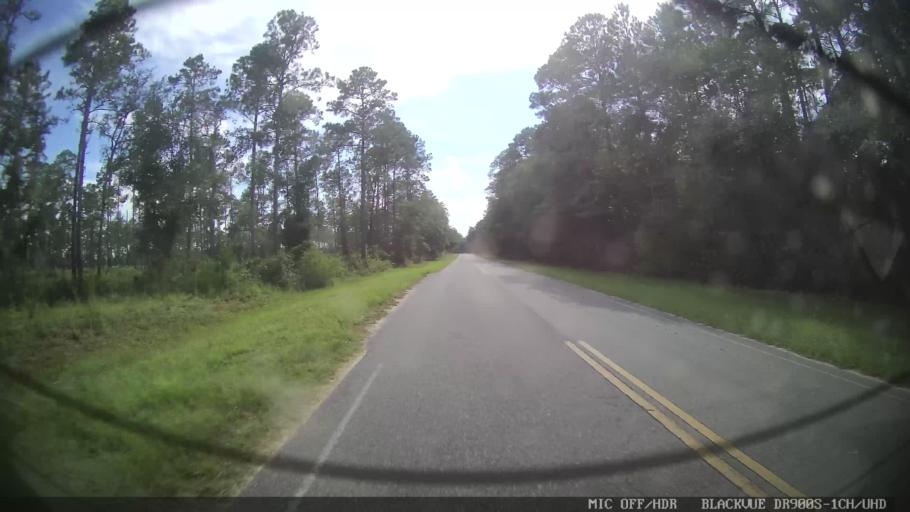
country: US
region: Georgia
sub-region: Echols County
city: Statenville
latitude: 30.6249
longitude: -83.2002
